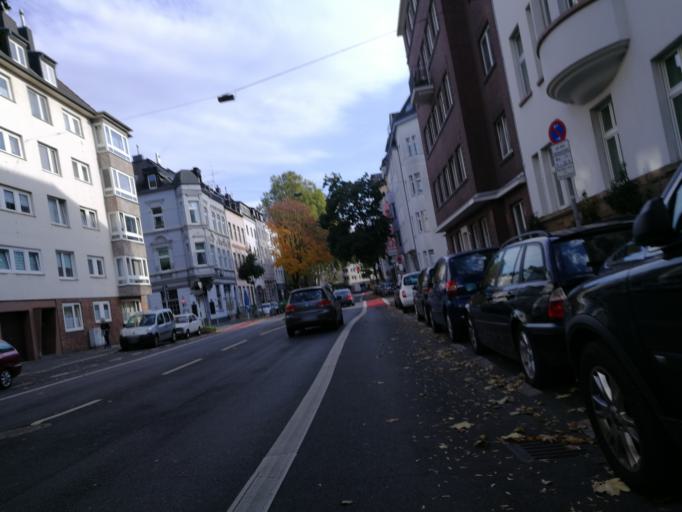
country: DE
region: North Rhine-Westphalia
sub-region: Regierungsbezirk Dusseldorf
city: Dusseldorf
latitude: 51.2149
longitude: 6.7682
